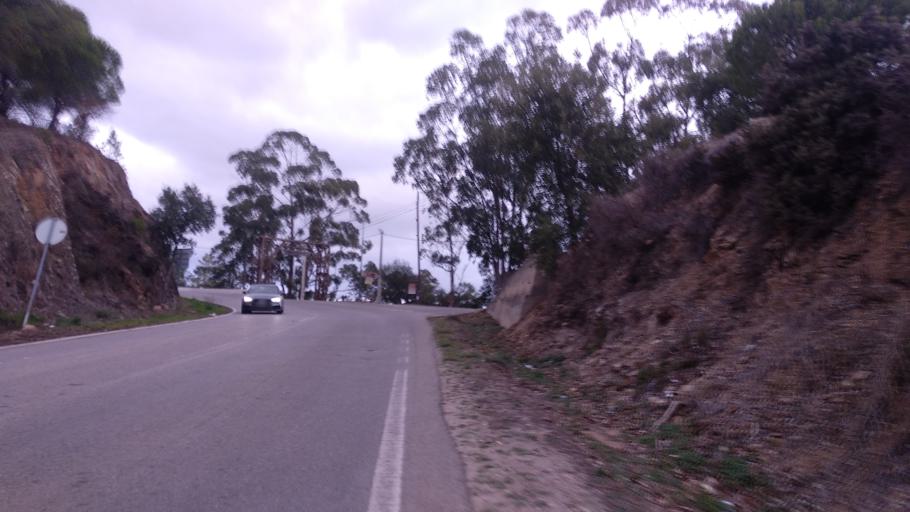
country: PT
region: Faro
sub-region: Sao Bras de Alportel
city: Sao Bras de Alportel
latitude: 37.1793
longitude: -7.9103
